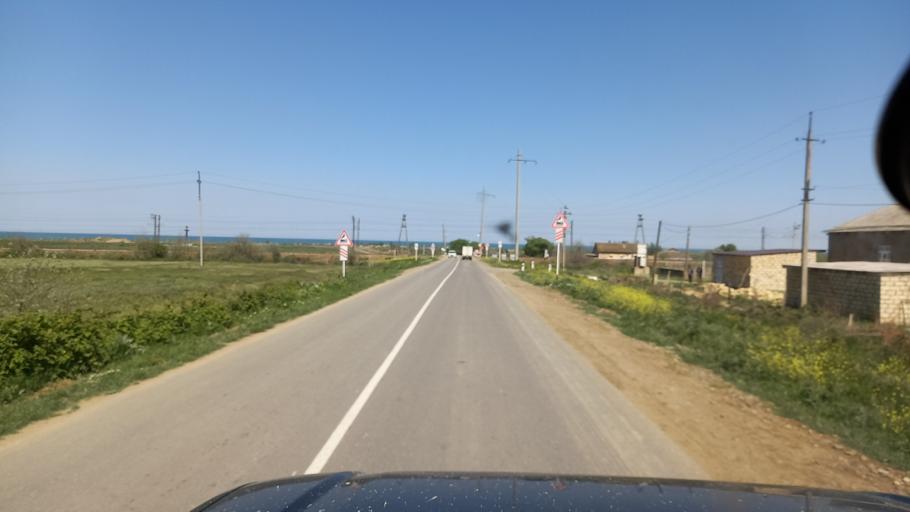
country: RU
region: Dagestan
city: Khazar
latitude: 41.9437
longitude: 48.3418
